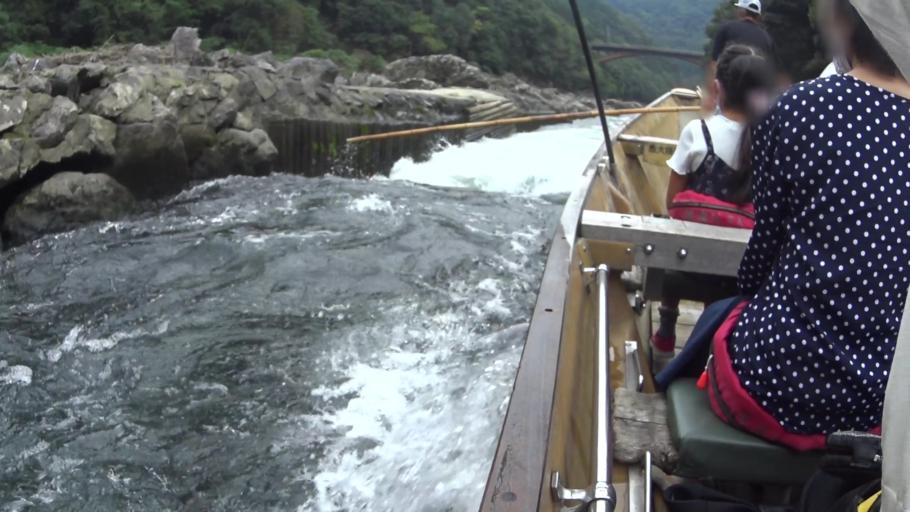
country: JP
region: Kyoto
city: Kameoka
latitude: 35.0233
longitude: 135.6209
